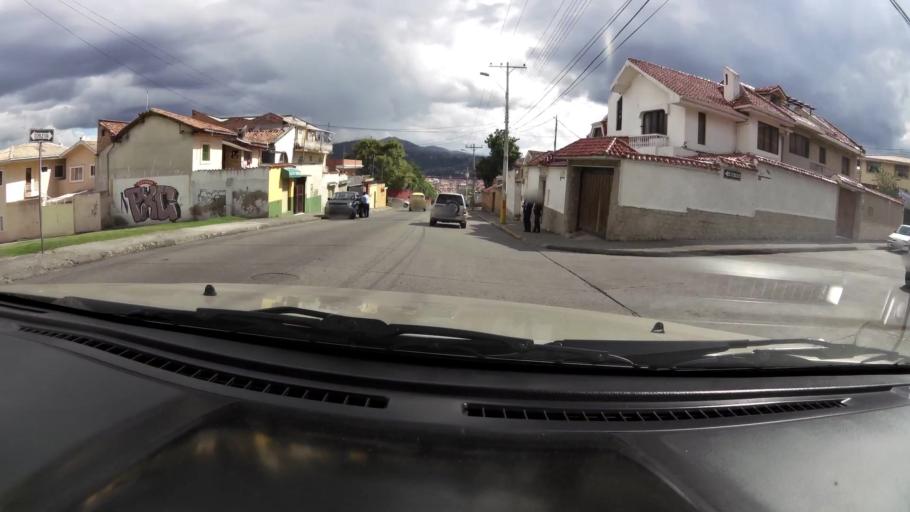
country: EC
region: Azuay
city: Cuenca
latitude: -2.8869
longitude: -78.9992
